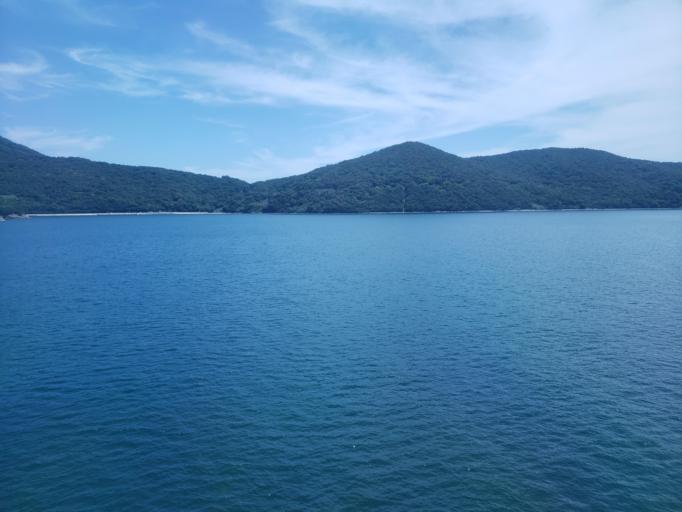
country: JP
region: Kagawa
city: Tonosho
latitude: 34.4406
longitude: 134.3177
